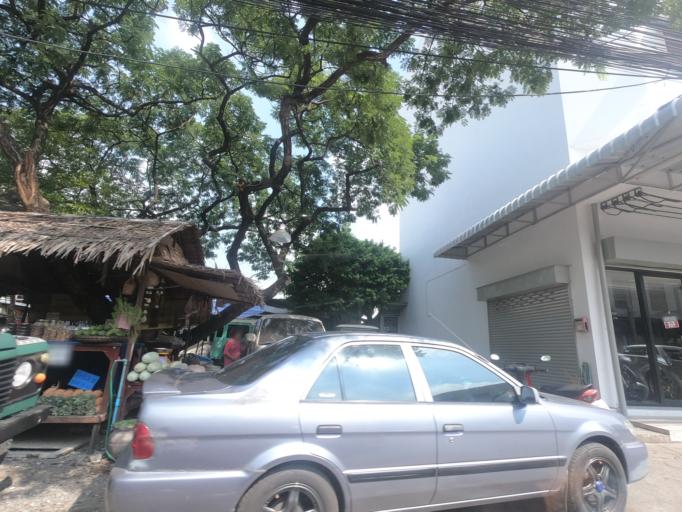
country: TH
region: Bangkok
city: Lat Phrao
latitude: 13.8211
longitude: 100.5985
